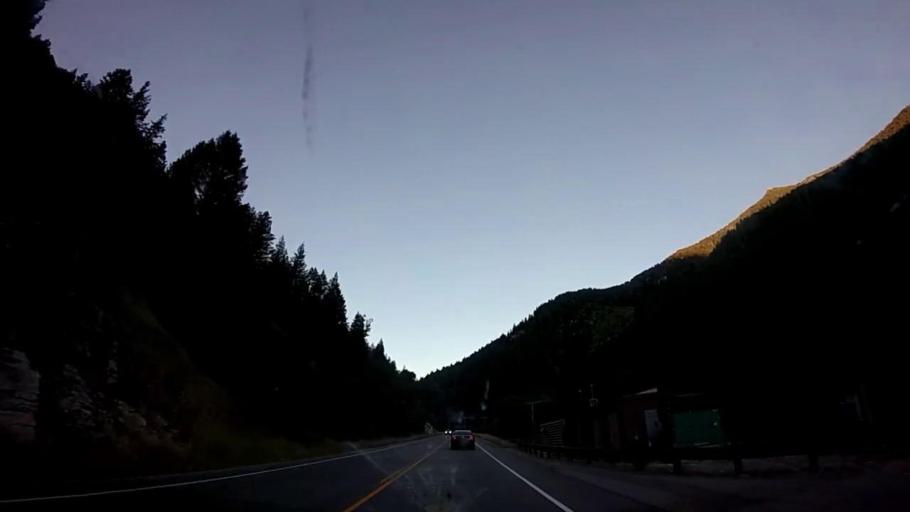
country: US
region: Utah
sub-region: Salt Lake County
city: Mount Olympus
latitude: 40.6424
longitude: -111.6812
